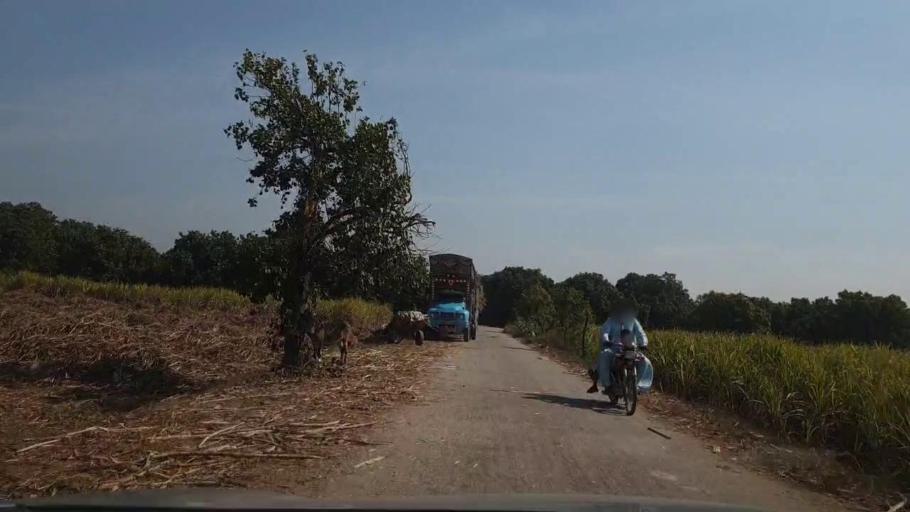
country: PK
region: Sindh
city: Tando Adam
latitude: 25.6269
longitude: 68.7354
